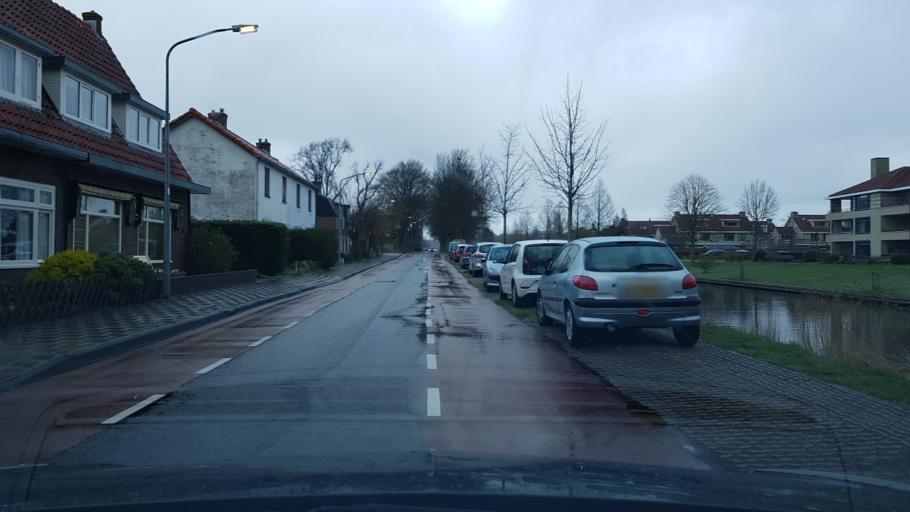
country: NL
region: North Holland
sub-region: Gemeente Bloemendaal
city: Bennebroek
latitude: 52.3217
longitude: 4.5860
